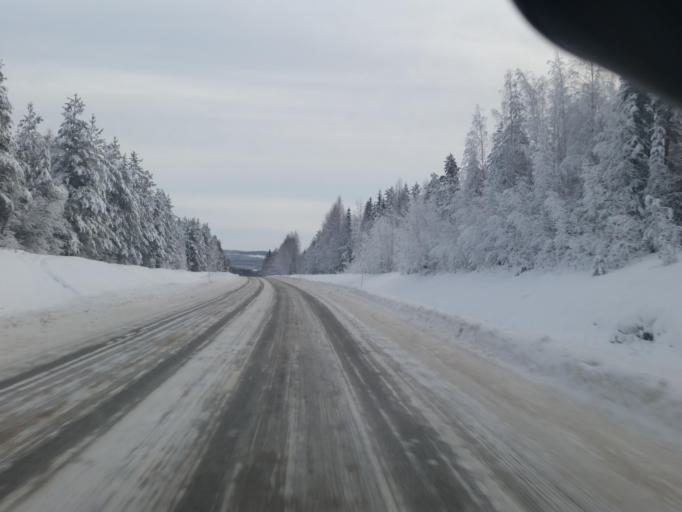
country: SE
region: Norrbotten
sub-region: Pitea Kommun
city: Norrfjarden
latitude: 65.6347
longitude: 21.3595
